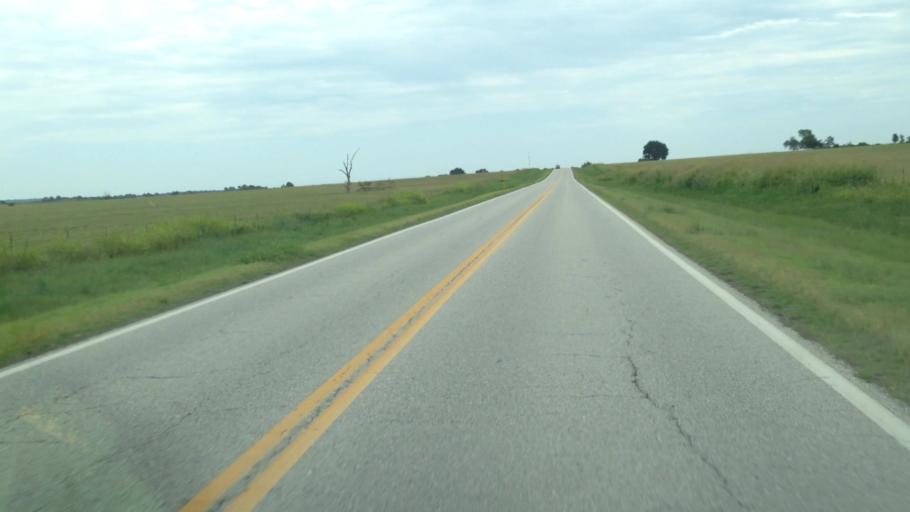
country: US
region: Kansas
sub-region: Labette County
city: Chetopa
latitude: 36.8505
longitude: -95.1210
